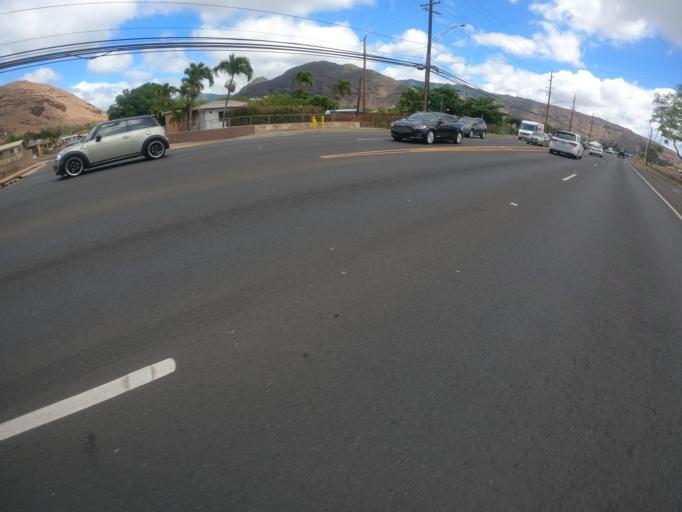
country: US
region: Hawaii
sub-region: Honolulu County
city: Nanakuli
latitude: 21.3947
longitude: -158.1608
